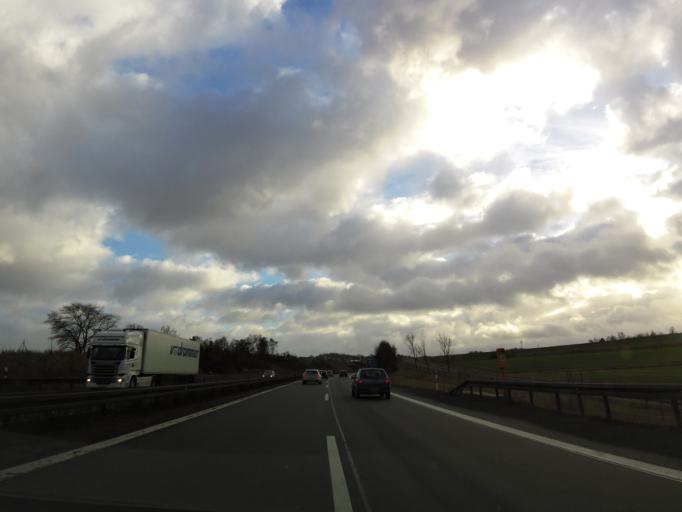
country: DE
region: Bavaria
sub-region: Upper Franconia
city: Thierstein
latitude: 50.1171
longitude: 12.0961
